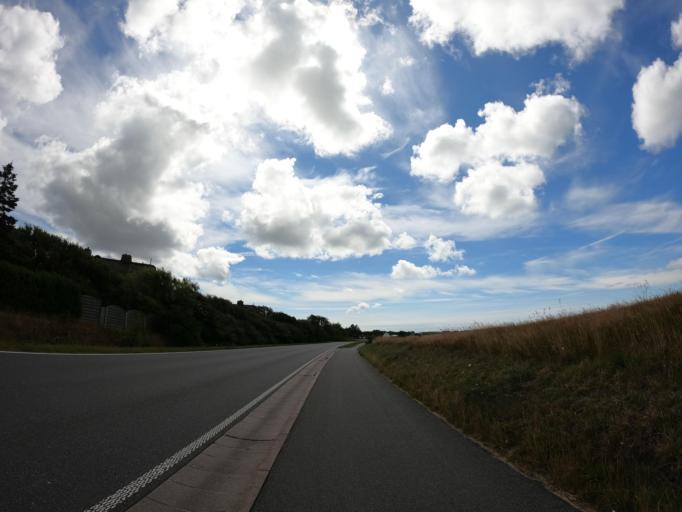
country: DE
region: Schleswig-Holstein
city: Keitum
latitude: 54.8983
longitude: 8.3651
